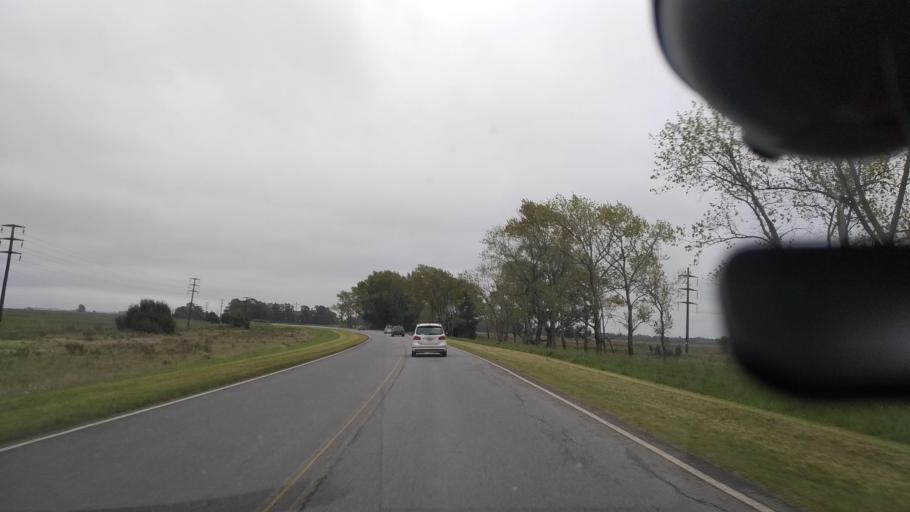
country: AR
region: Buenos Aires
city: Veronica
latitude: -35.3800
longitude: -57.3683
